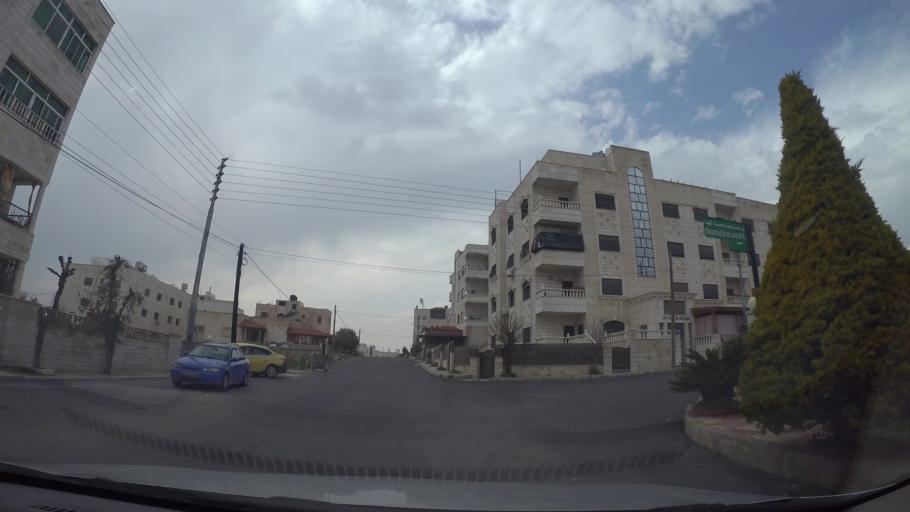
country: JO
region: Amman
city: Umm as Summaq
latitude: 31.8813
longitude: 35.8604
